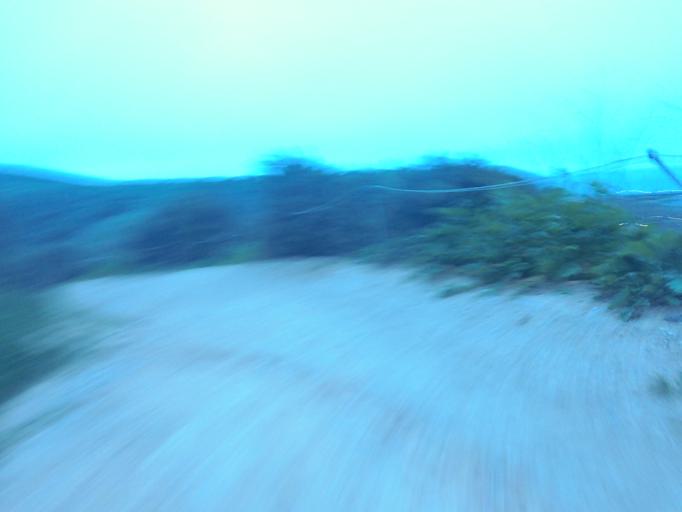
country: US
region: California
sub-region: Orange County
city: Laguna Beach
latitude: 33.5630
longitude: -117.8197
